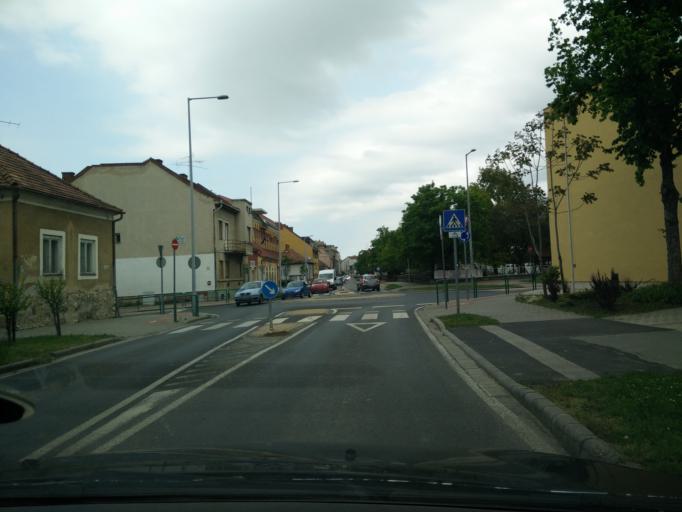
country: HU
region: Zala
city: Zalaegerszeg
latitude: 46.8411
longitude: 16.8417
